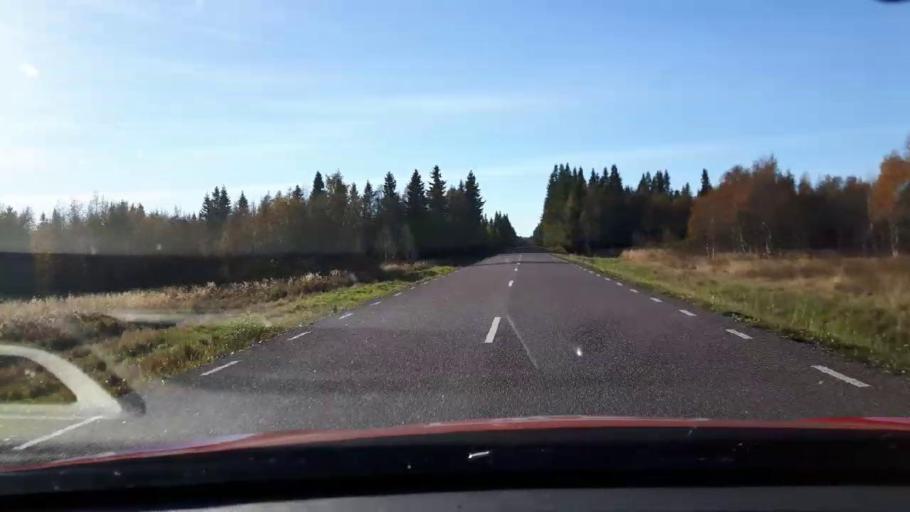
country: SE
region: Jaemtland
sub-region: Stroemsunds Kommun
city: Stroemsund
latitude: 63.8465
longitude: 15.2910
